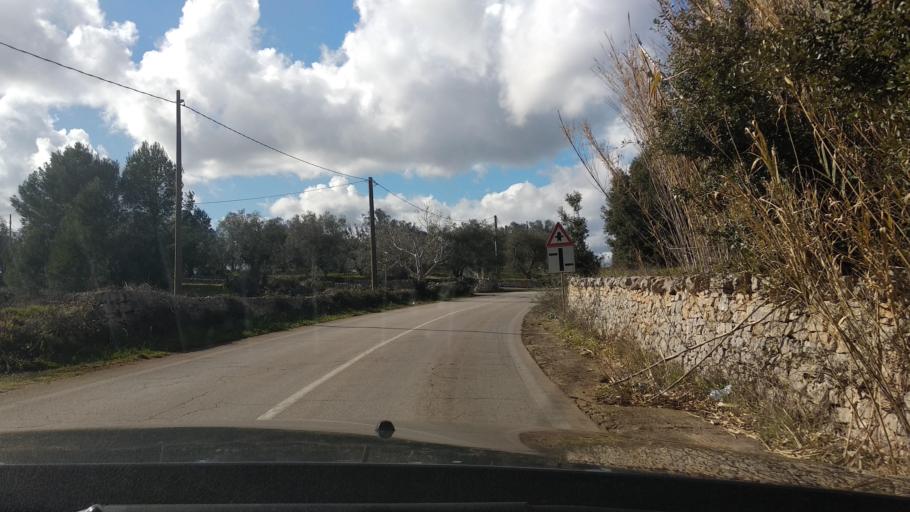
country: IT
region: Apulia
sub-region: Provincia di Brindisi
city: Casalini
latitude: 40.7076
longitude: 17.5147
